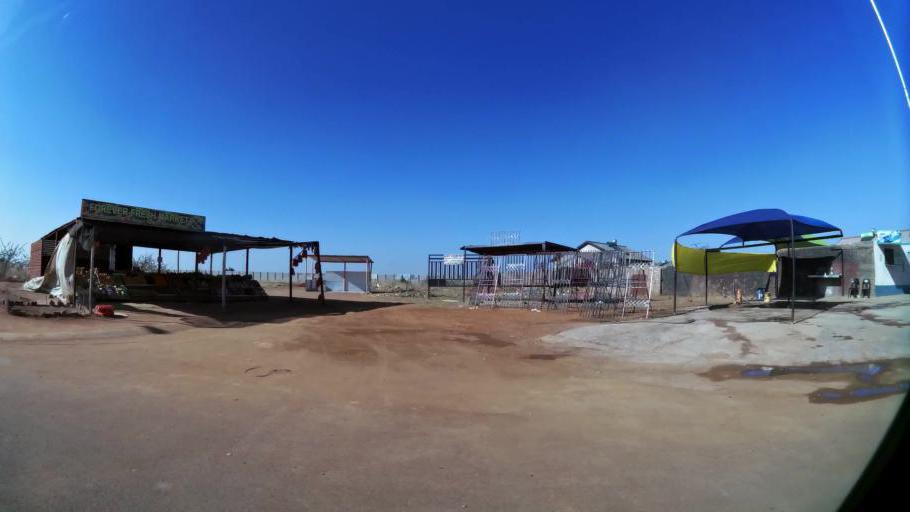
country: ZA
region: Gauteng
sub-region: City of Tshwane Metropolitan Municipality
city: Mabopane
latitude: -25.5578
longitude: 28.0960
